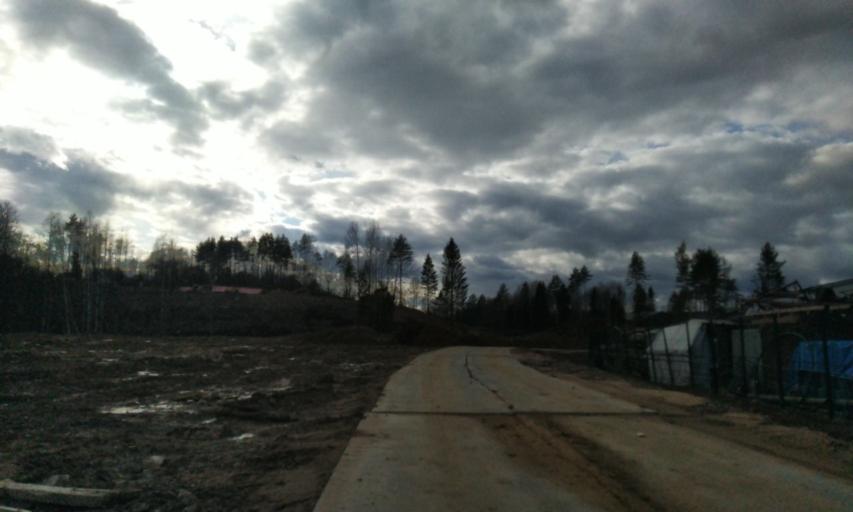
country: RU
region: Leningrad
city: Bugry
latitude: 60.1263
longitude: 30.4352
